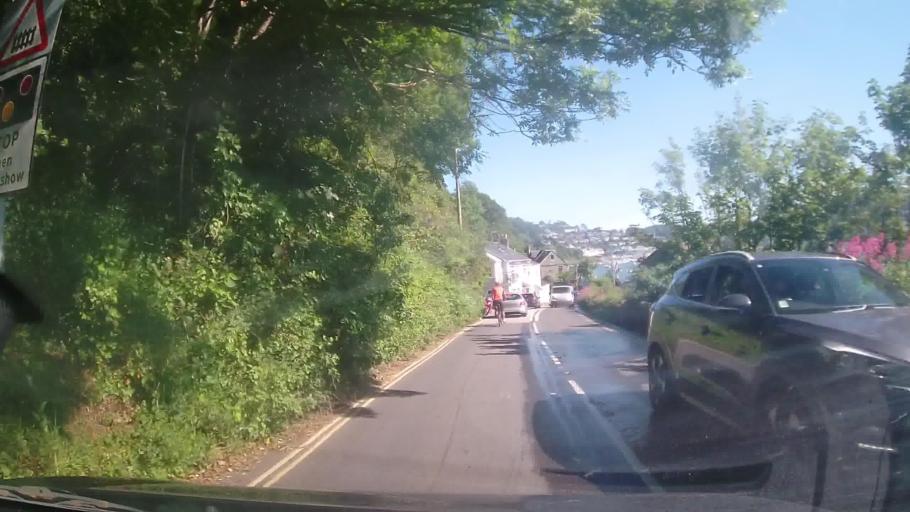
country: GB
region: England
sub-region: Devon
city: Dartmouth
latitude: 50.3608
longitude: -3.5732
